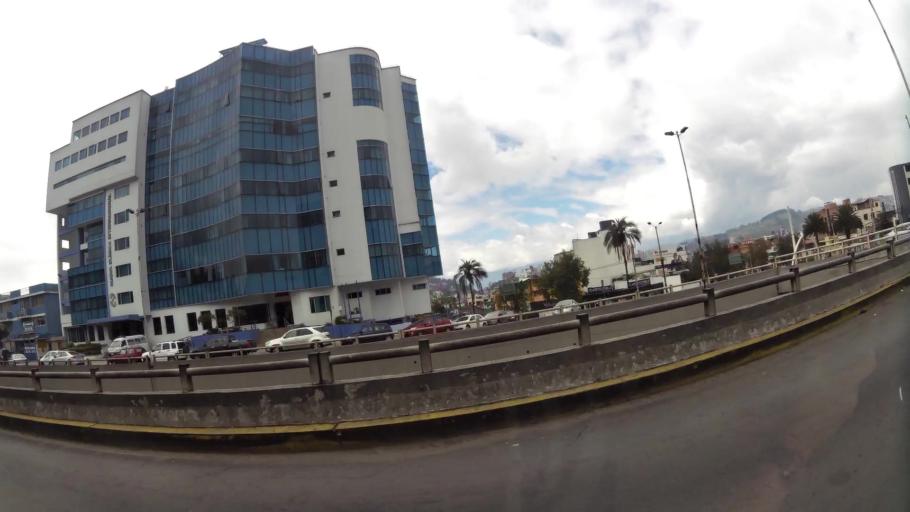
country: EC
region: Pichincha
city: Quito
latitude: -0.1860
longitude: -78.4956
